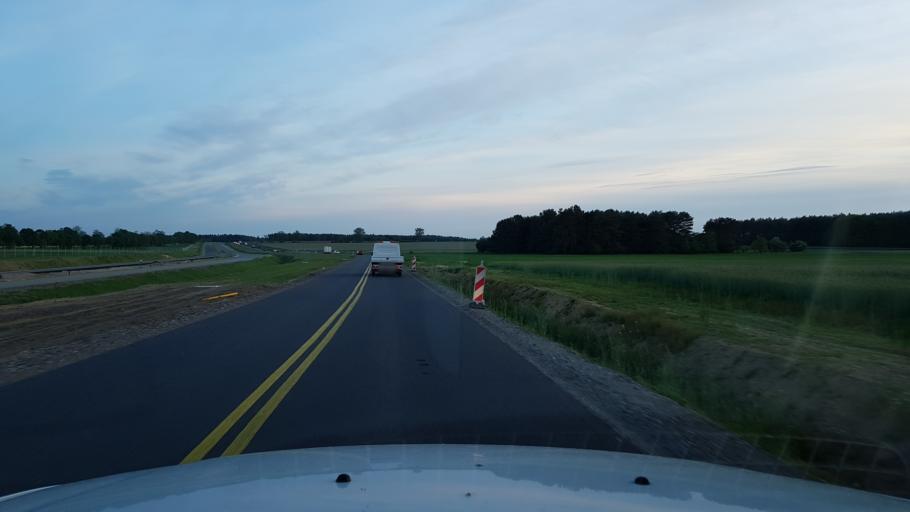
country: PL
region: West Pomeranian Voivodeship
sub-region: Powiat goleniowski
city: Nowogard
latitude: 53.7116
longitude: 15.1770
